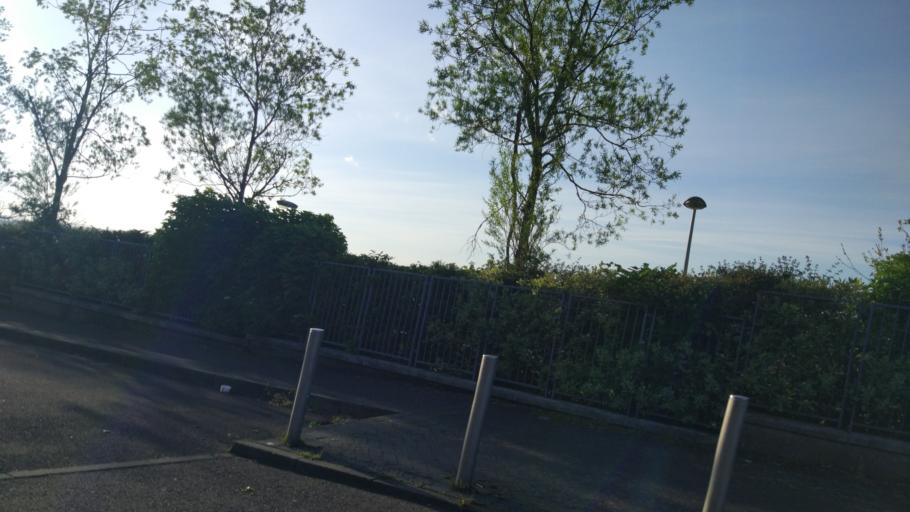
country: IE
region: Munster
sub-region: County Cork
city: Cork
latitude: 51.9124
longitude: -8.4627
